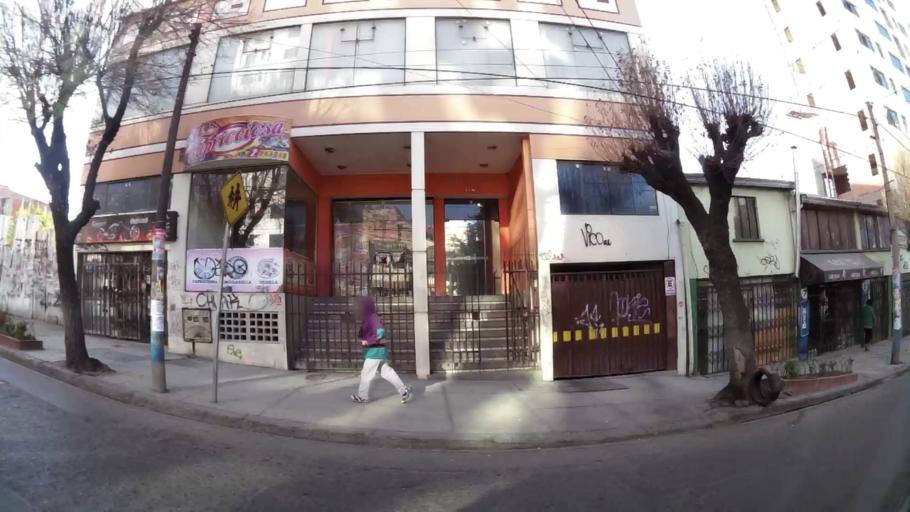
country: BO
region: La Paz
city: La Paz
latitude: -16.4913
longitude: -68.1215
